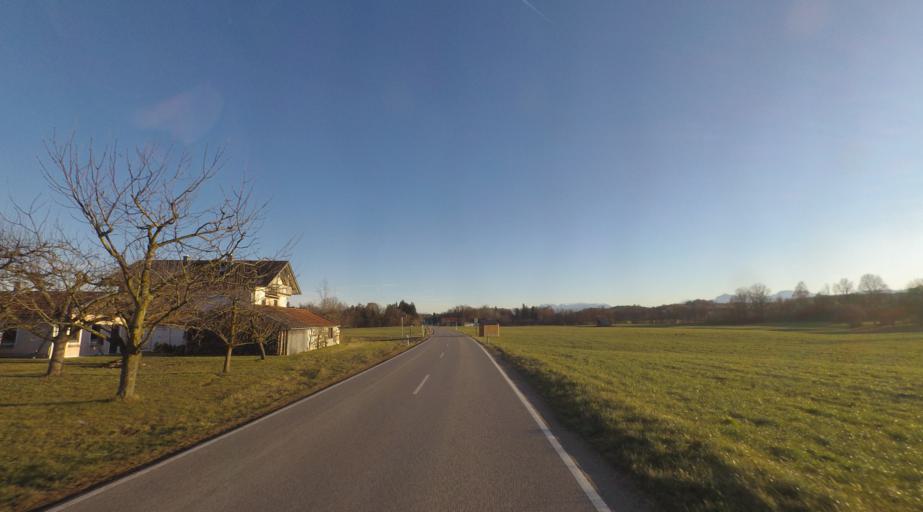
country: DE
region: Bavaria
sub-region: Upper Bavaria
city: Kirchanschoring
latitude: 47.9723
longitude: 12.8163
